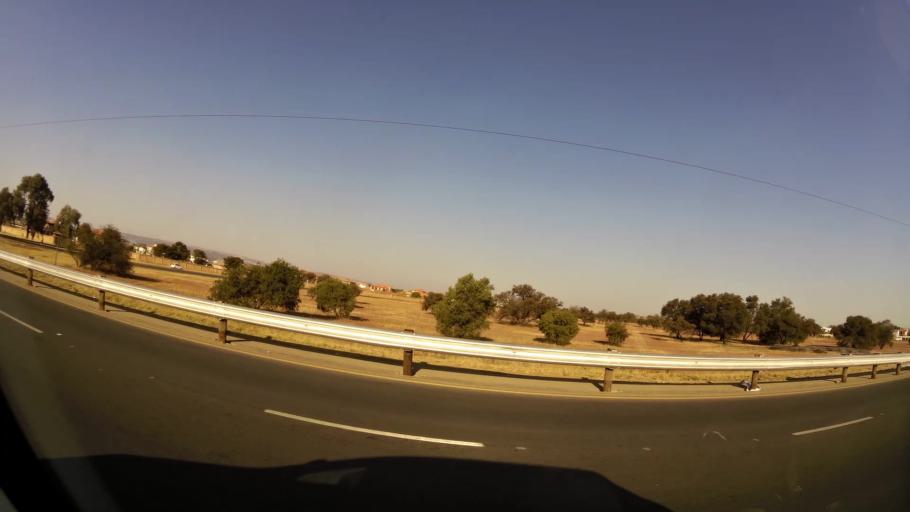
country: ZA
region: Gauteng
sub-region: City of Tshwane Metropolitan Municipality
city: Pretoria
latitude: -25.7578
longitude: 28.3639
